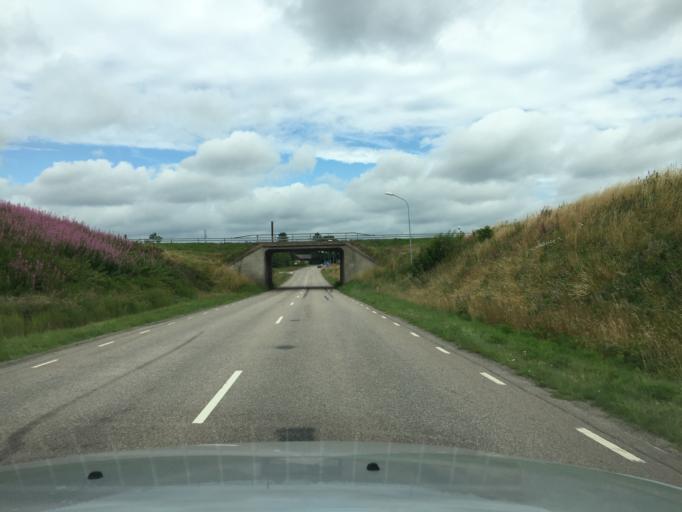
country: SE
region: Skane
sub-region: Hassleholms Kommun
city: Sosdala
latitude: 56.0306
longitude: 13.6837
